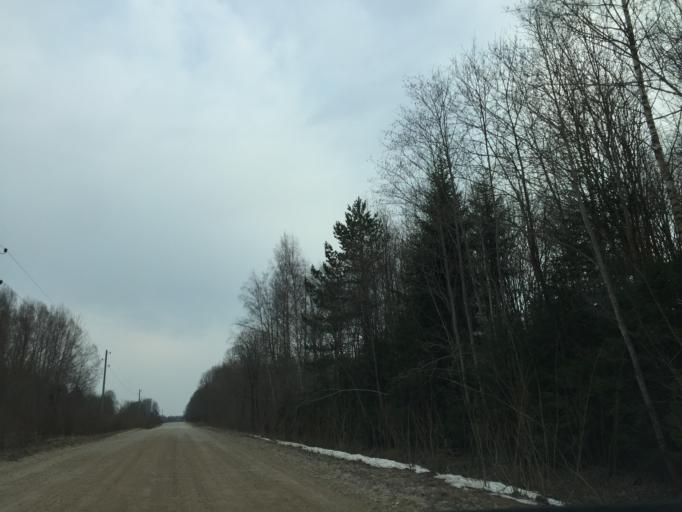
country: LV
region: Priekuli
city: Priekuli
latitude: 57.1820
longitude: 25.4714
